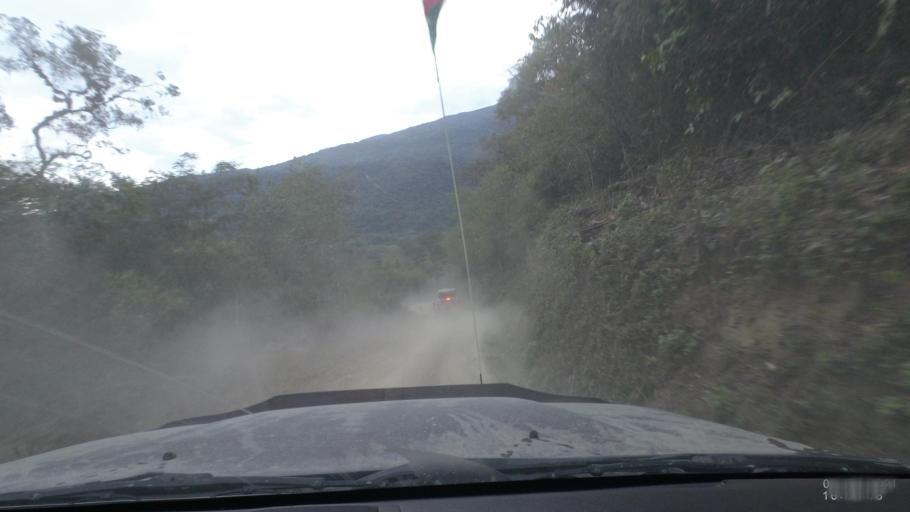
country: BO
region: La Paz
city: Quime
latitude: -16.5128
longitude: -66.7643
